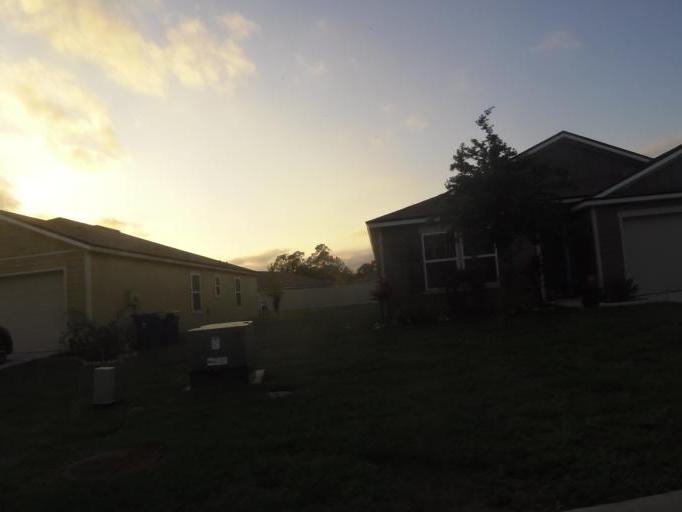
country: US
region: Florida
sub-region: Duval County
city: Jacksonville
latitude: 30.4706
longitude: -81.6243
